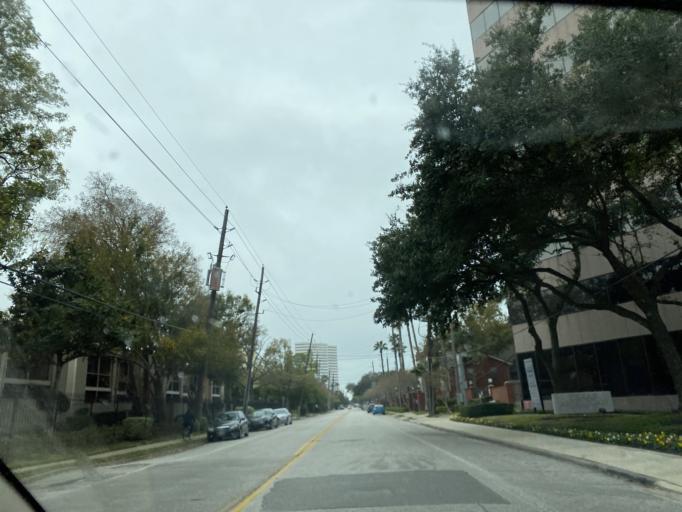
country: US
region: Texas
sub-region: Harris County
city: Hunters Creek Village
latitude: 29.7457
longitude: -95.4795
